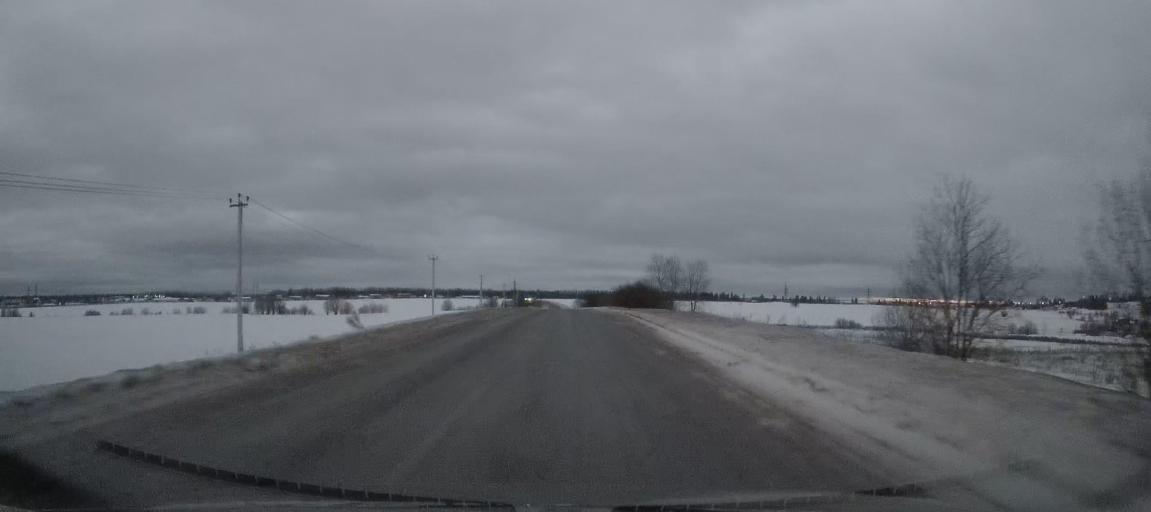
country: RU
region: Leningrad
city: Taytsy
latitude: 59.6877
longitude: 30.1302
